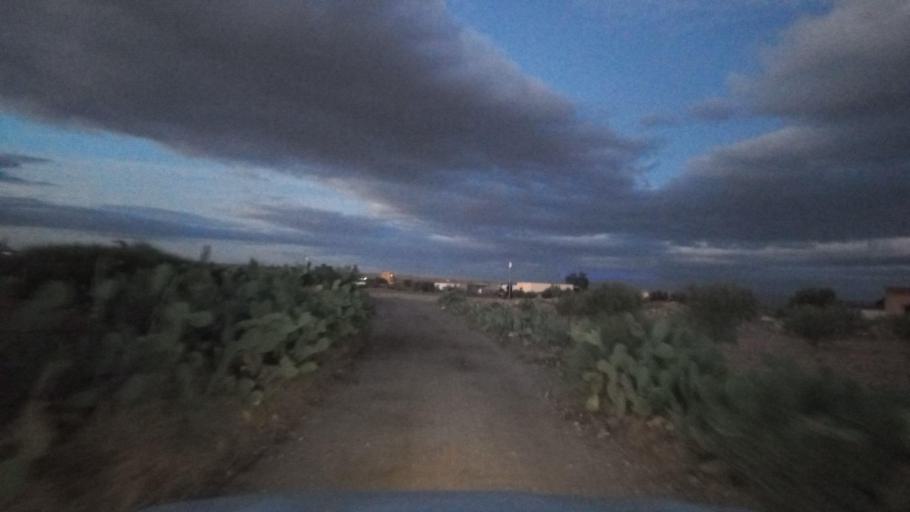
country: TN
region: Al Qasrayn
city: Kasserine
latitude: 35.2574
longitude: 8.9414
